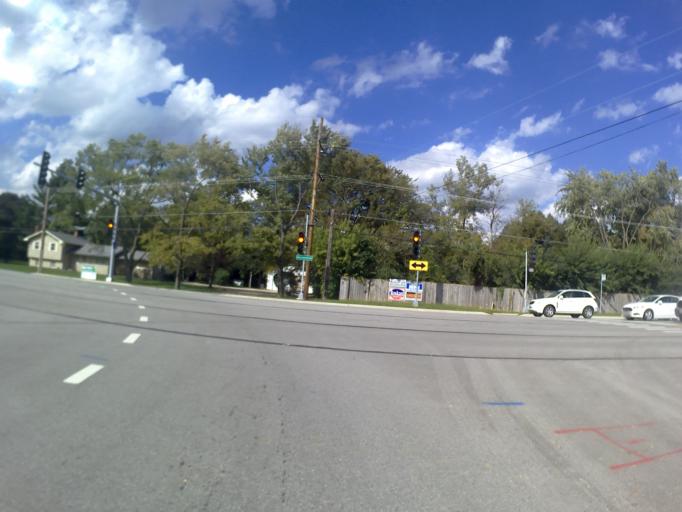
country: US
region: Illinois
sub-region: DuPage County
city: Lisle
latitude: 41.8082
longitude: -88.0914
